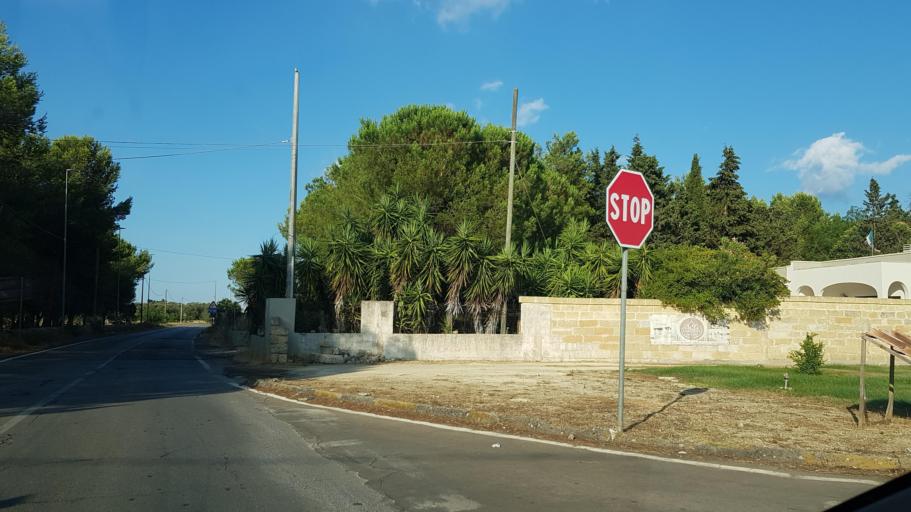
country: IT
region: Apulia
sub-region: Provincia di Lecce
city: Montesano Salentino
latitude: 39.9736
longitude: 18.3268
